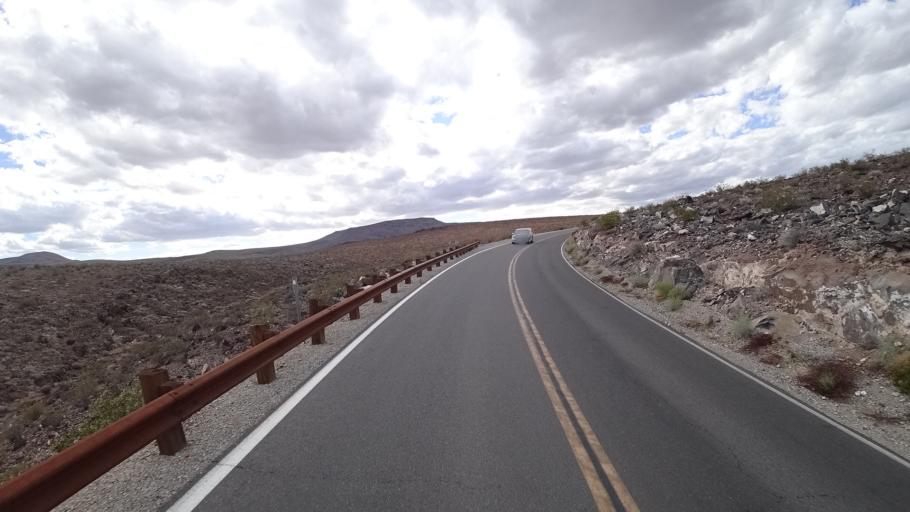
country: US
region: California
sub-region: Inyo County
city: Lone Pine
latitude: 36.3491
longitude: -117.5492
